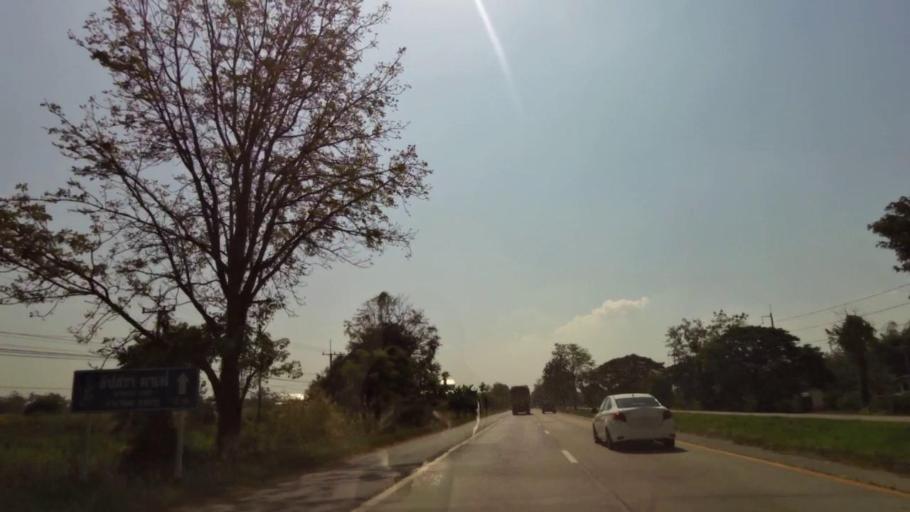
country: TH
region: Phichit
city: Wachira Barami
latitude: 16.6052
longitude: 100.1484
